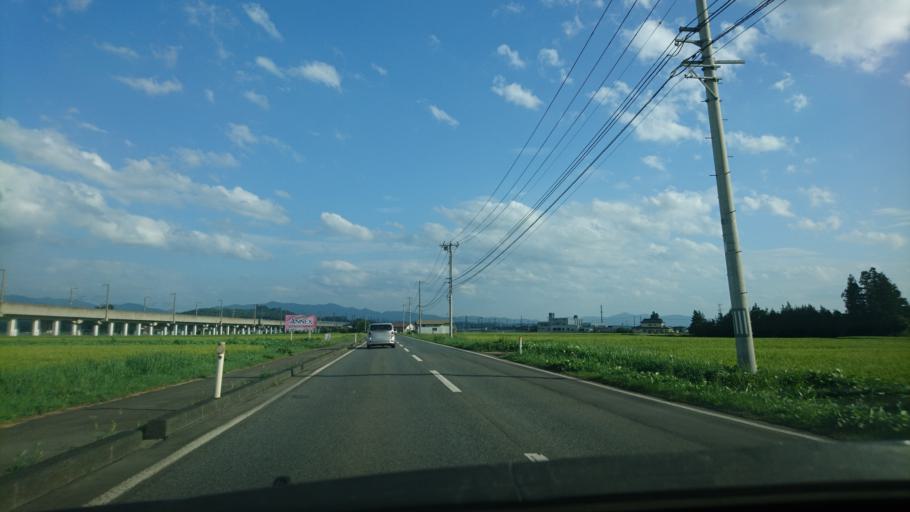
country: JP
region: Iwate
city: Mizusawa
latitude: 39.1680
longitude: 141.1790
